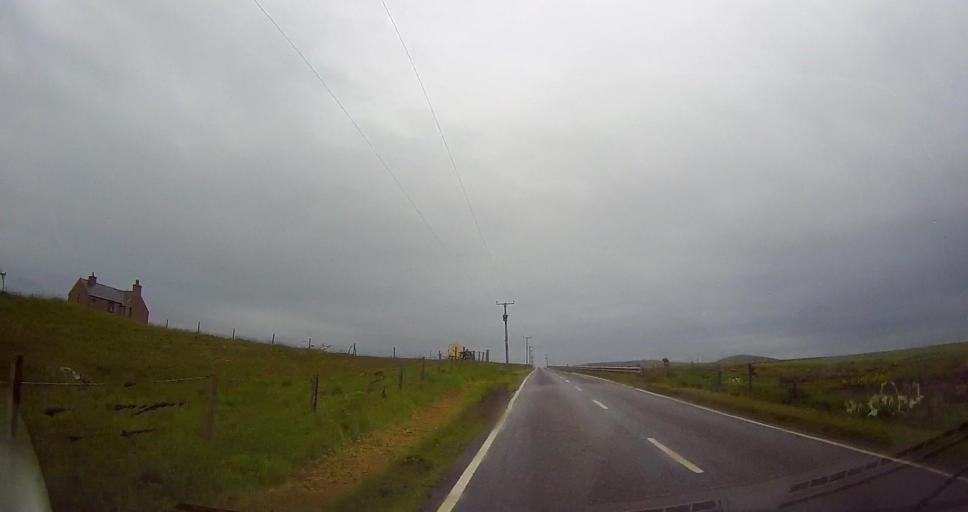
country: GB
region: Scotland
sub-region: Orkney Islands
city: Stromness
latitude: 59.0262
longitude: -3.2936
